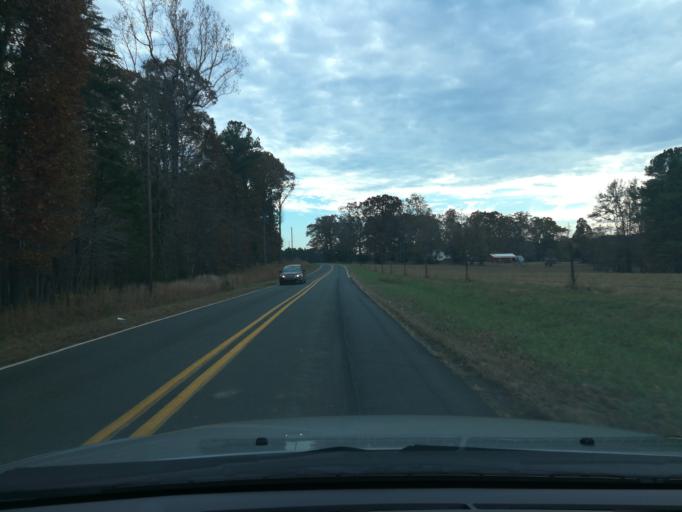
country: US
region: North Carolina
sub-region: Orange County
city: Hillsborough
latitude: 36.0049
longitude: -79.0465
